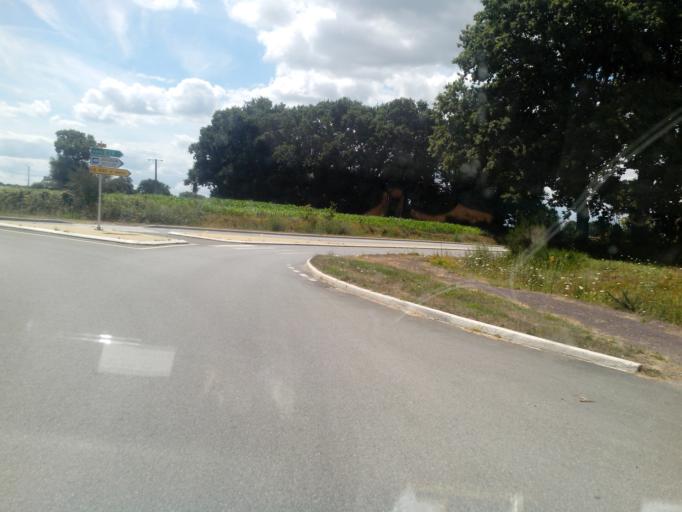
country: FR
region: Brittany
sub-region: Departement du Morbihan
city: Josselin
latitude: 47.9475
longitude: -2.5544
